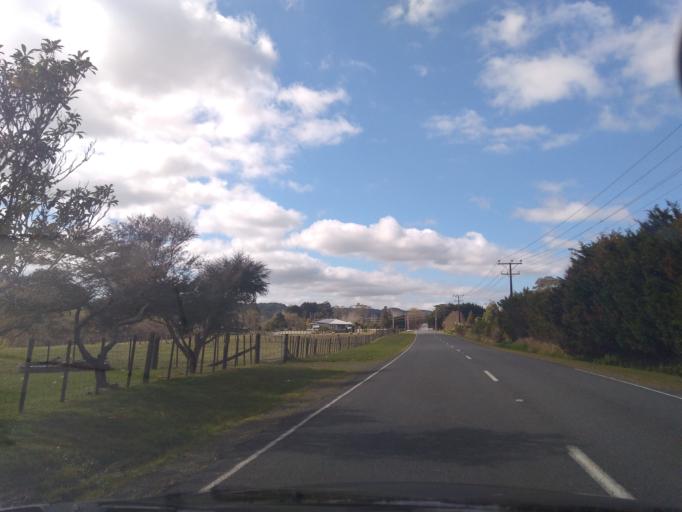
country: NZ
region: Northland
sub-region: Whangarei
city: Whangarei
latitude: -35.6996
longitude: 174.3466
